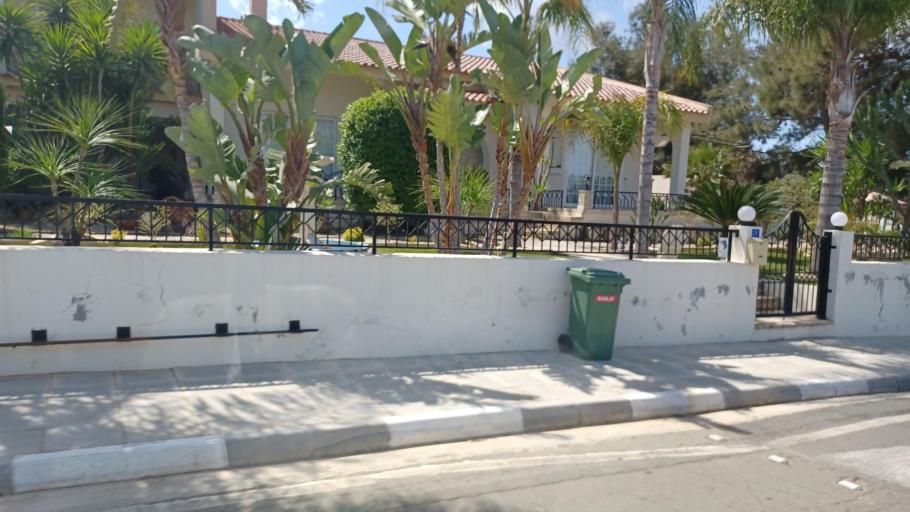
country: CY
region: Lefkosia
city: Astromeritis
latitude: 35.0803
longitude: 33.0143
